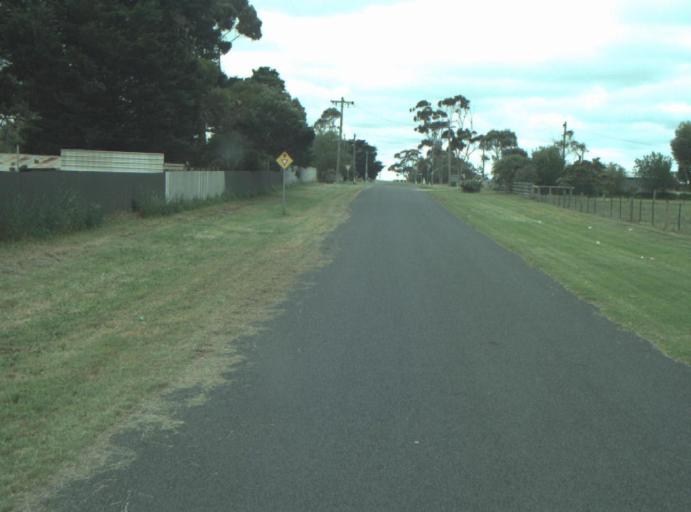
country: AU
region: Victoria
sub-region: Greater Geelong
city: Bell Post Hill
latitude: -38.0583
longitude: 144.3188
